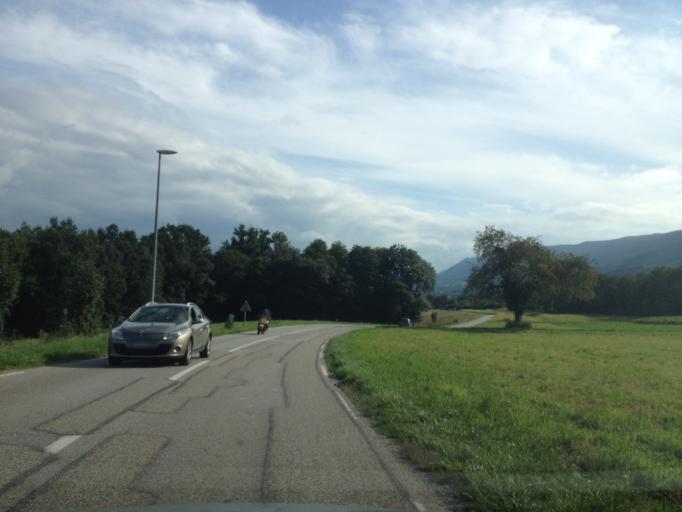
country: FR
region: Rhone-Alpes
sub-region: Departement de la Savoie
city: Le Bourget-du-Lac
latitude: 45.6250
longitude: 5.8628
